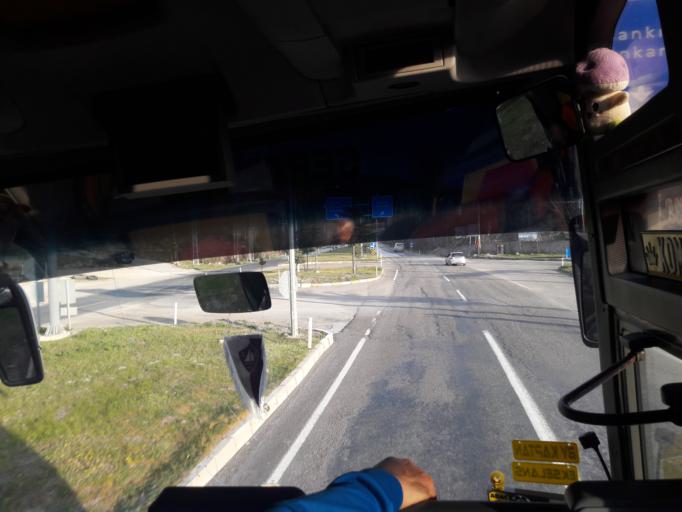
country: TR
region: Cankiri
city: Korgun
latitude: 40.7343
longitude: 33.5205
